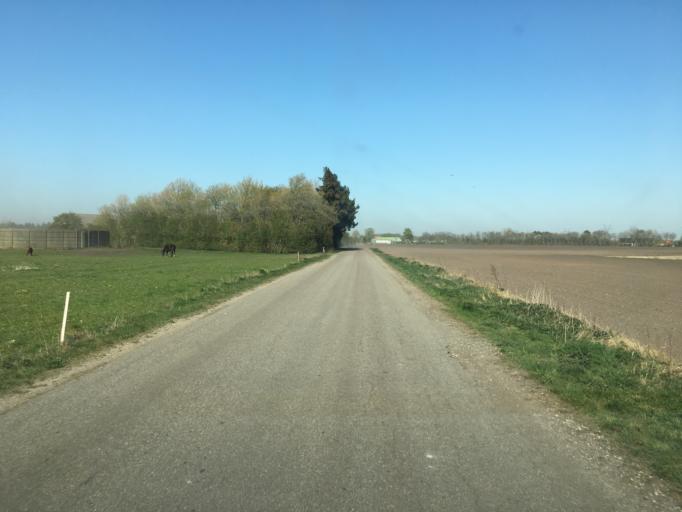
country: DK
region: South Denmark
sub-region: Aabenraa Kommune
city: Rodekro
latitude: 55.0805
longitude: 9.2617
